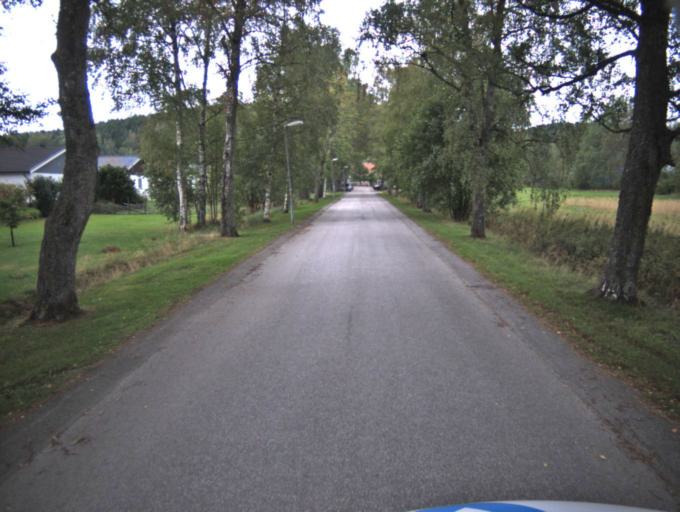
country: SE
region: Vaestra Goetaland
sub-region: Ulricehamns Kommun
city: Ulricehamn
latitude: 57.8070
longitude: 13.4095
